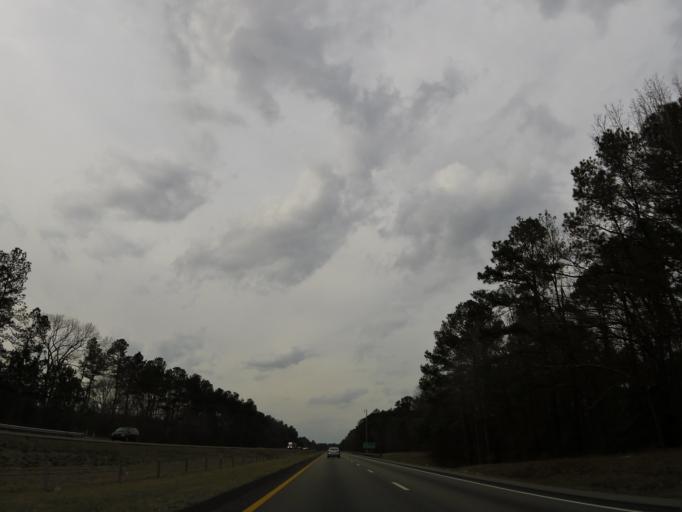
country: US
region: South Carolina
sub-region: Calhoun County
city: Oak Grove
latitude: 33.6811
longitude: -80.9037
